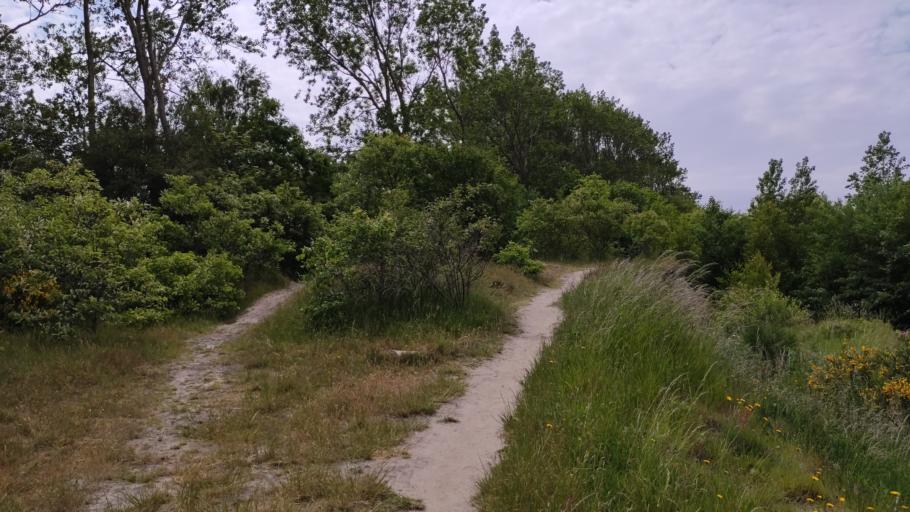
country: DE
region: Mecklenburg-Vorpommern
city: Bastorf
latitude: 54.1330
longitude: 11.6509
